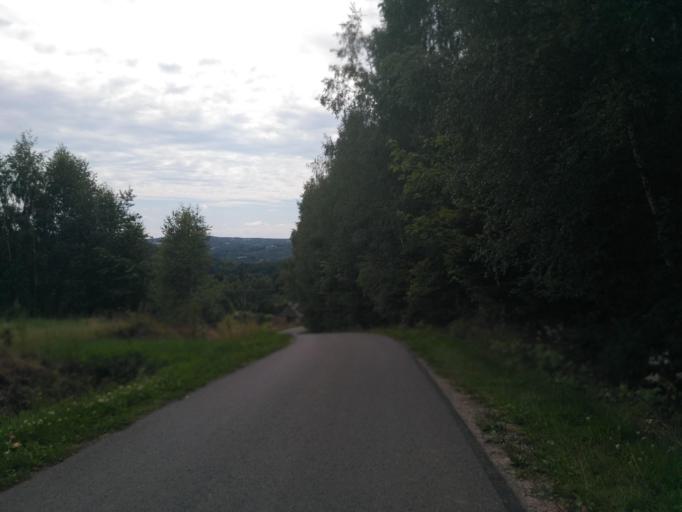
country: PL
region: Subcarpathian Voivodeship
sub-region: Powiat strzyzowski
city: Gwoznica Gorna
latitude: 49.8530
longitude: 21.9724
